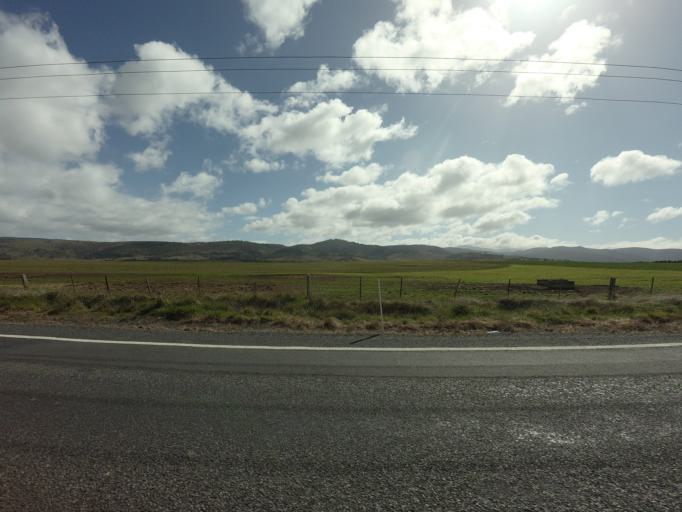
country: AU
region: Tasmania
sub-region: Northern Midlands
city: Evandale
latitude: -41.8023
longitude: 147.6875
